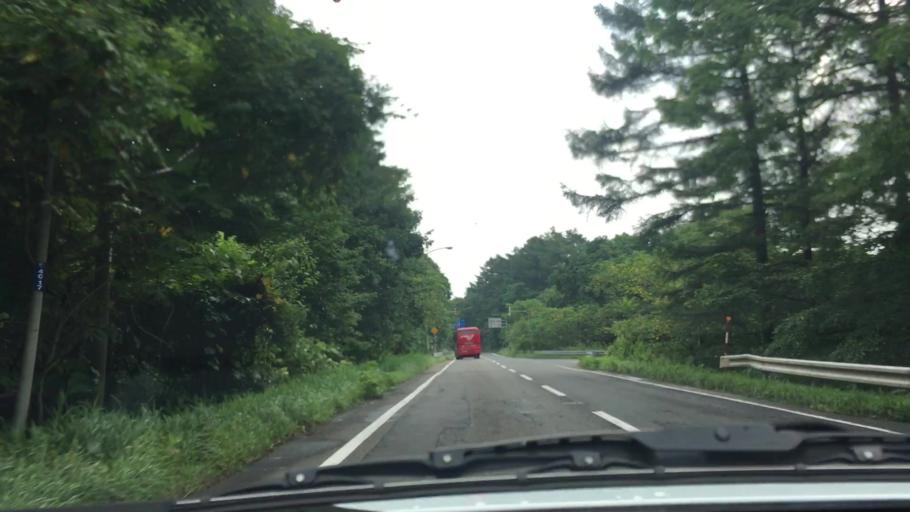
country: JP
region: Hokkaido
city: Chitose
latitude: 42.9442
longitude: 141.7443
